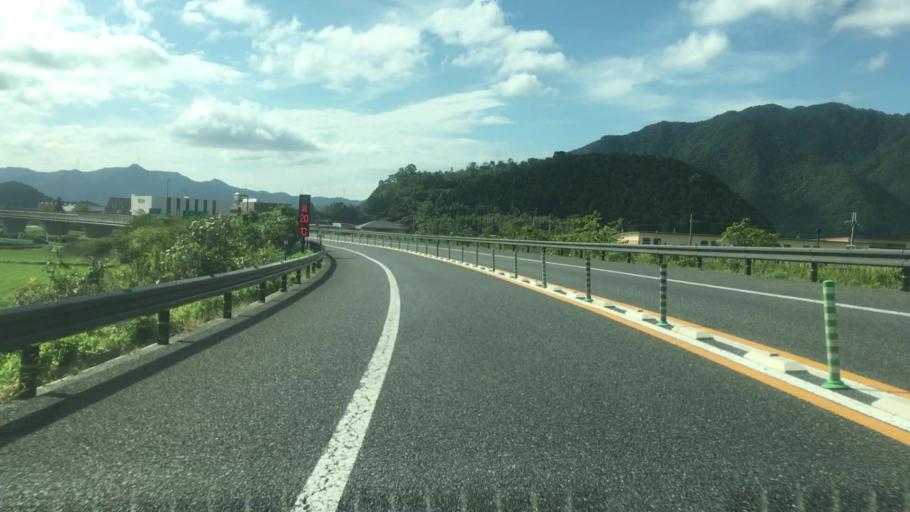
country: JP
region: Kyoto
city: Fukuchiyama
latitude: 35.1820
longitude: 135.0367
